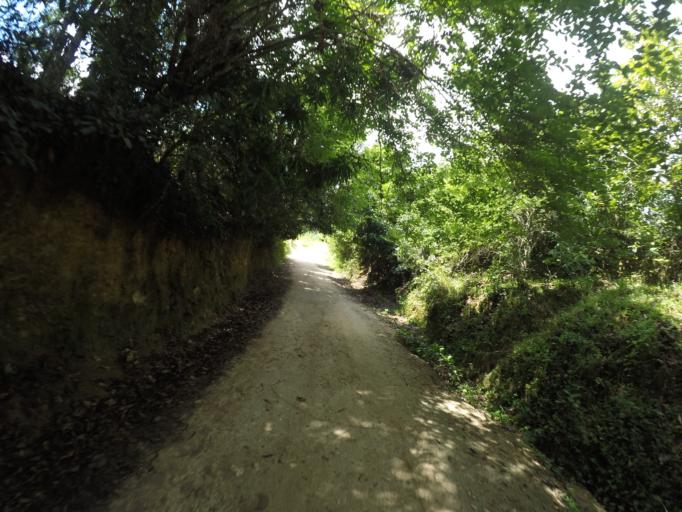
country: TZ
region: Pemba South
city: Mtambile
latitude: -5.3887
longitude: 39.7399
